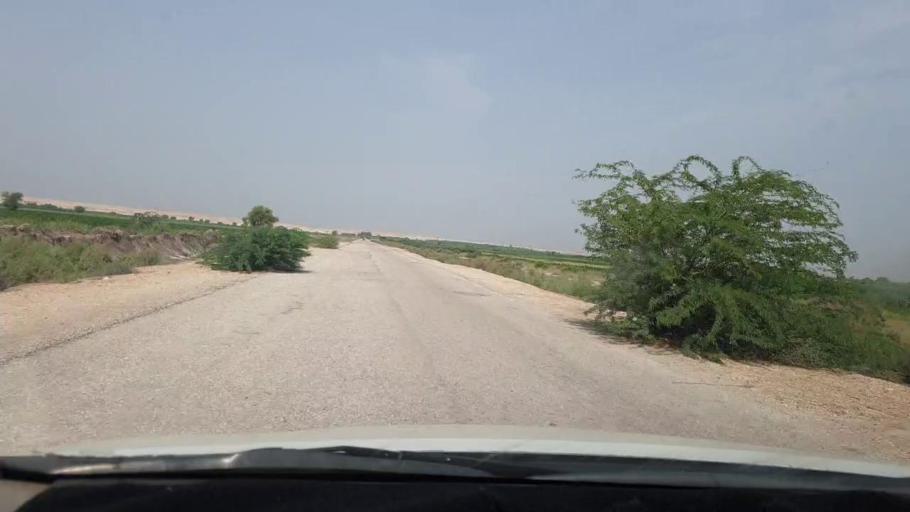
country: PK
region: Sindh
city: Rohri
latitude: 27.5947
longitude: 69.0007
